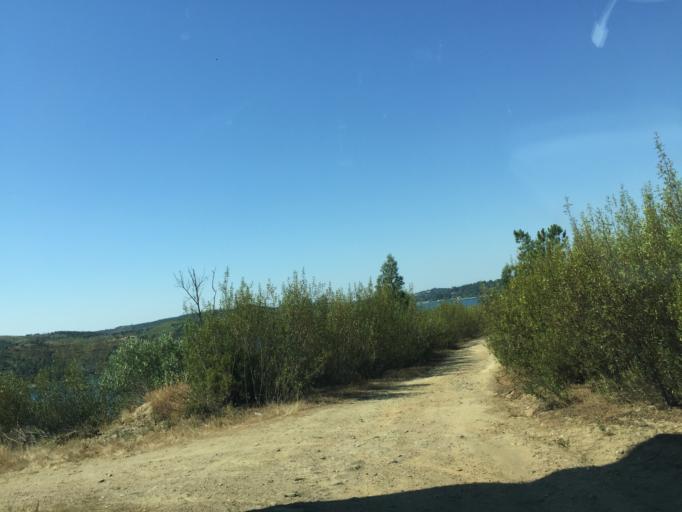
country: PT
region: Santarem
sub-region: Ferreira do Zezere
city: Ferreira do Zezere
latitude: 39.5756
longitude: -8.2759
